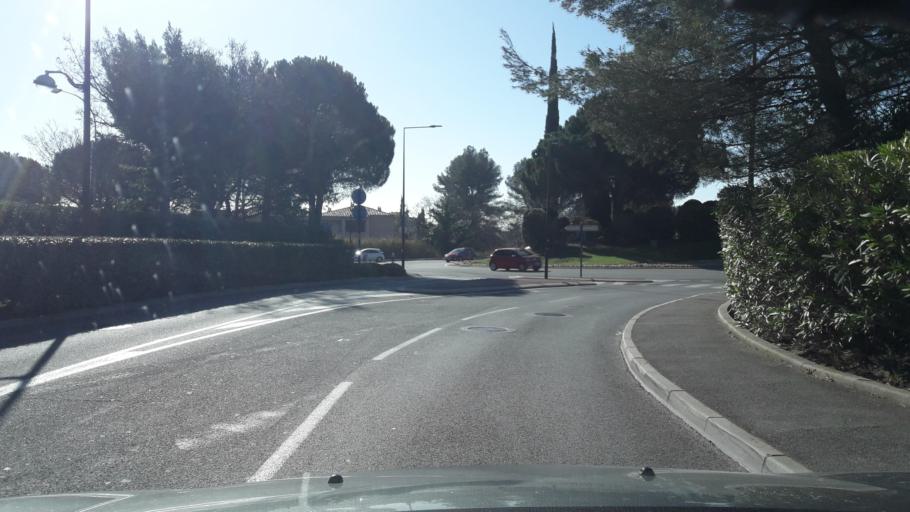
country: FR
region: Provence-Alpes-Cote d'Azur
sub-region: Departement du Var
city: Frejus
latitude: 43.4387
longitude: 6.7490
